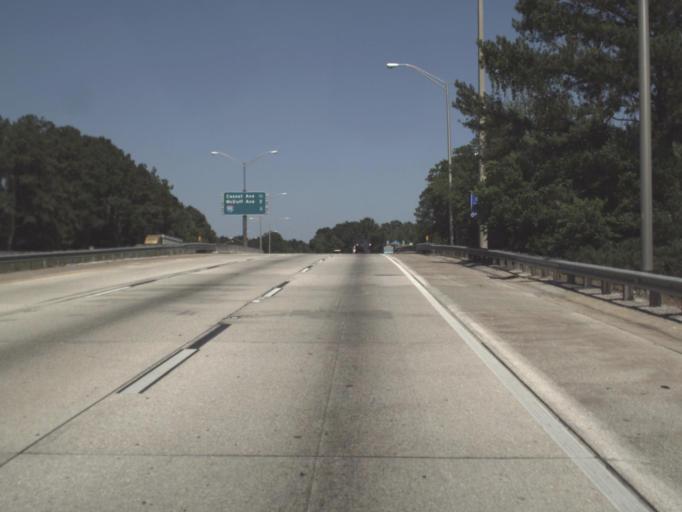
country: US
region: Florida
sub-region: Duval County
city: Jacksonville
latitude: 30.3154
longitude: -81.7447
